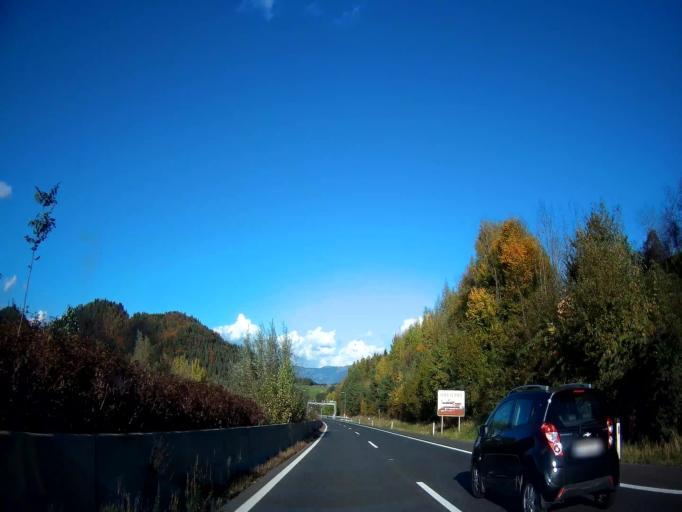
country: AT
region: Carinthia
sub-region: Politischer Bezirk Wolfsberg
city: Sankt Andrae
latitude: 46.7202
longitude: 14.7950
